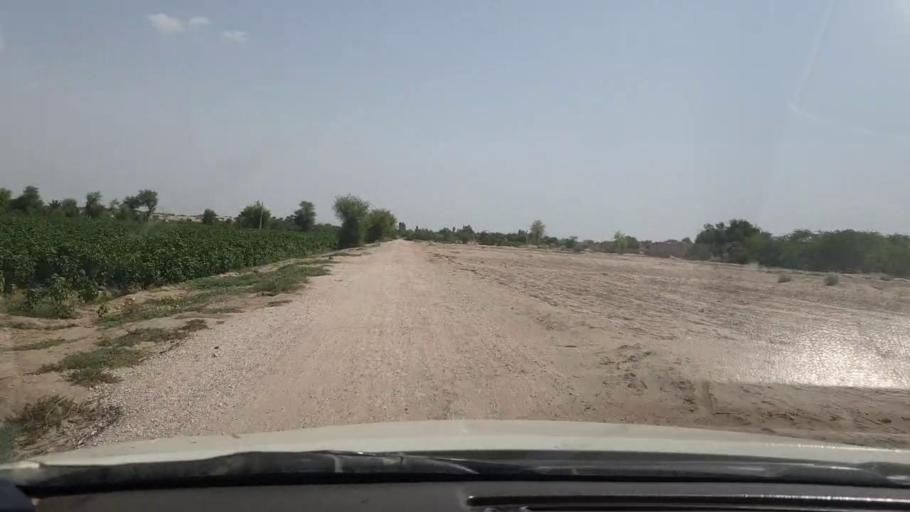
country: PK
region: Sindh
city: Rohri
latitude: 27.4683
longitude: 69.0789
